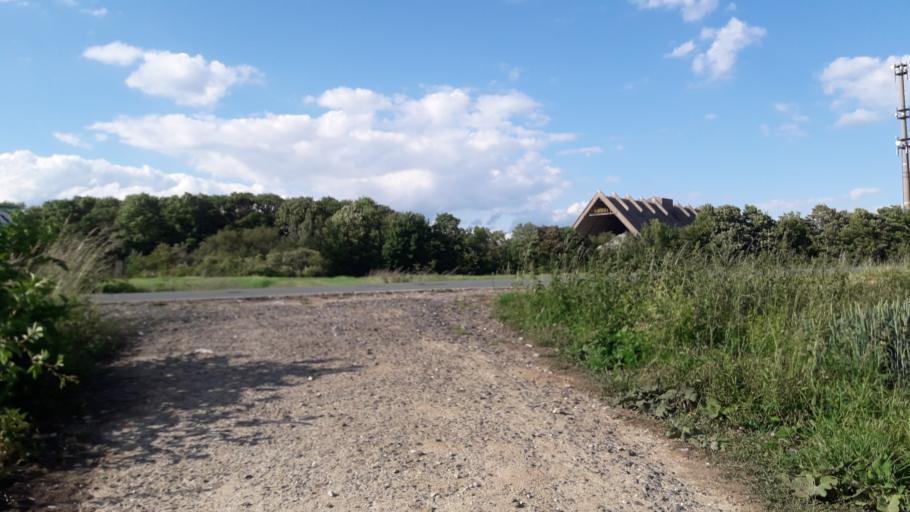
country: DE
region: North Rhine-Westphalia
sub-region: Regierungsbezirk Detmold
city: Paderborn
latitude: 51.6906
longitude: 8.7322
